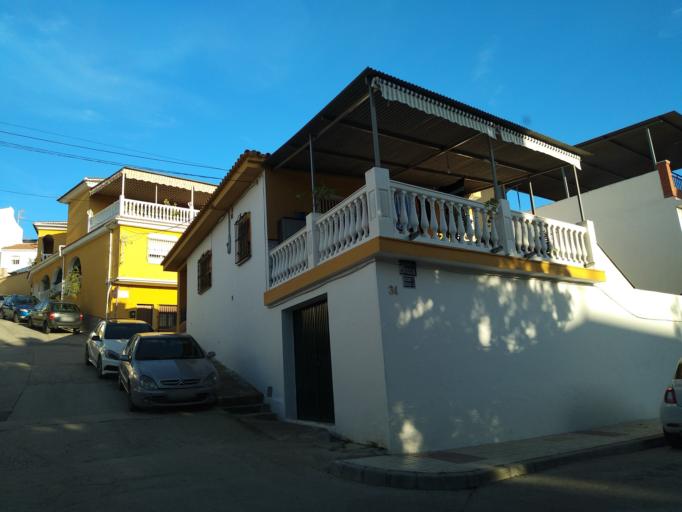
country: ES
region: Andalusia
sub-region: Provincia de Malaga
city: Estacion de Cartama
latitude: 36.7347
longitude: -4.5689
